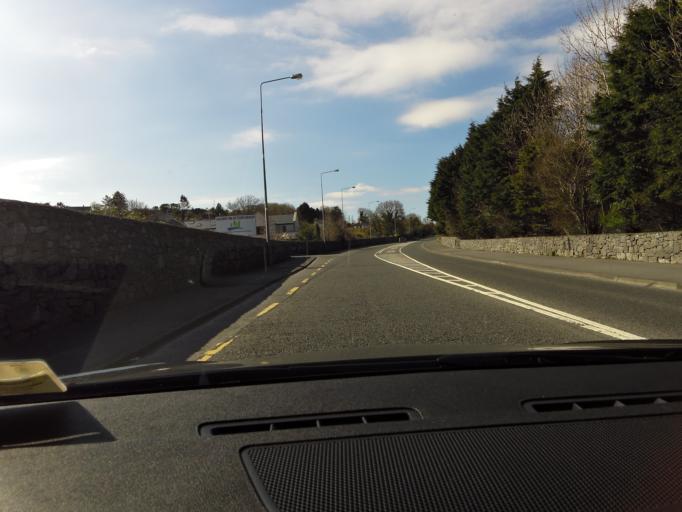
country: IE
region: Connaught
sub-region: County Galway
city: Gaillimh
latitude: 53.2916
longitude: -9.0831
